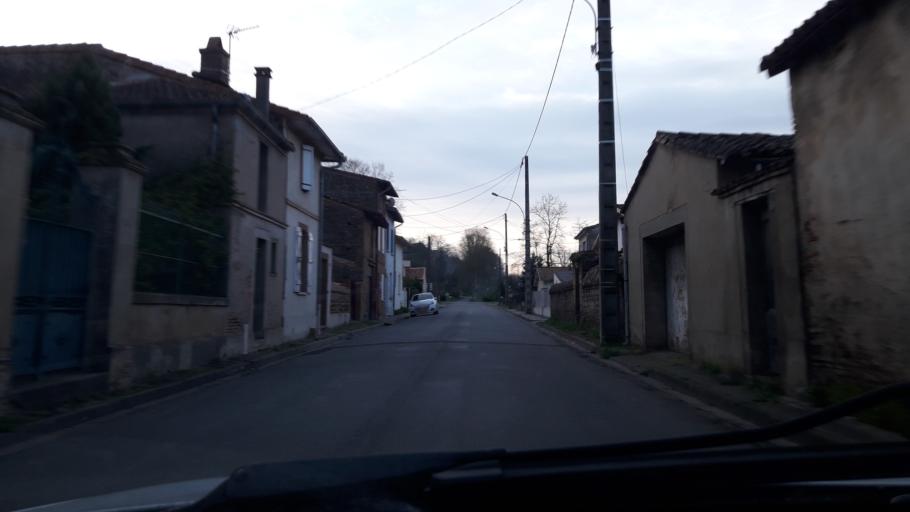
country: FR
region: Midi-Pyrenees
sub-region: Departement de la Haute-Garonne
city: Montesquieu-Volvestre
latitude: 43.2073
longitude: 1.2324
